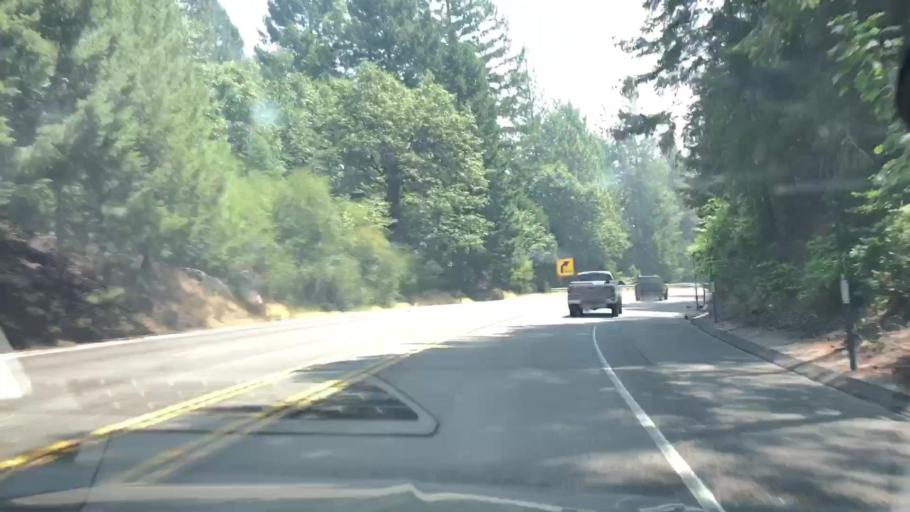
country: US
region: California
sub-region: El Dorado County
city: Pollock Pines
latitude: 38.7675
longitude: -120.5538
